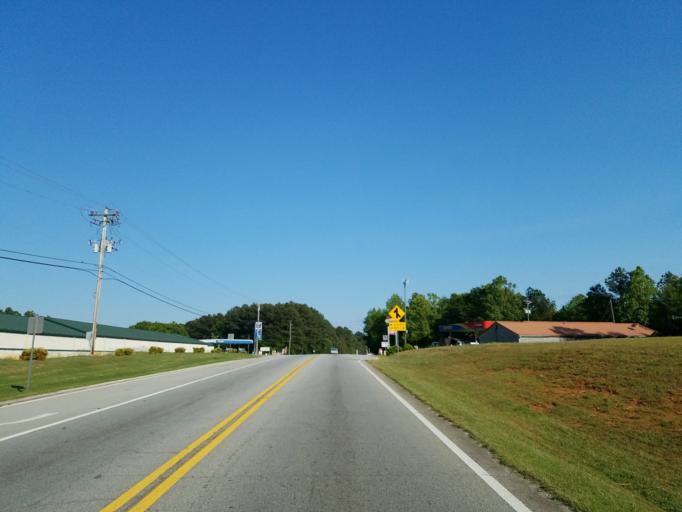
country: US
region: Georgia
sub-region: Carroll County
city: Villa Rica
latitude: 33.7552
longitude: -84.9365
